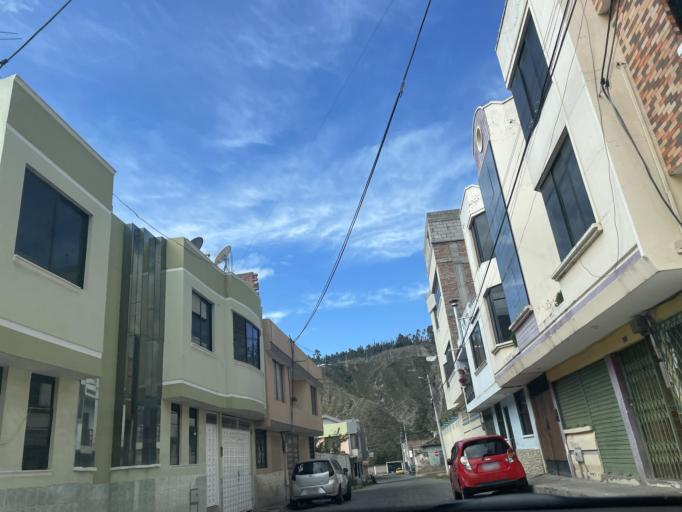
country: EC
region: Chimborazo
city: Guano
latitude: -1.6068
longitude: -78.6413
